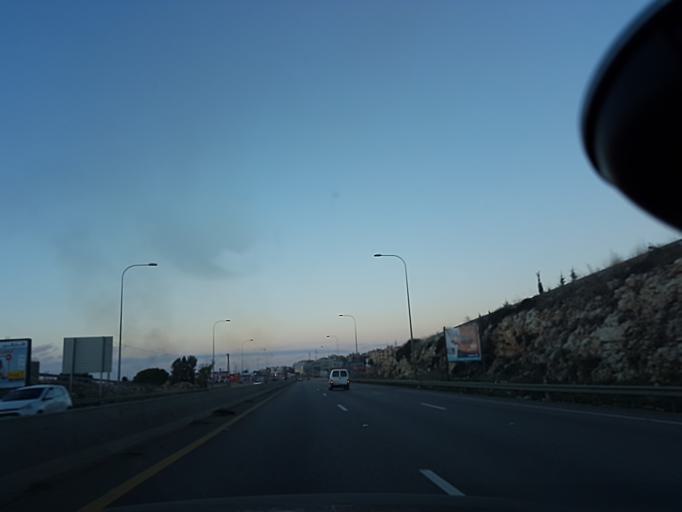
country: LB
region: Liban-Sud
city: Sidon
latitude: 33.6338
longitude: 35.4024
